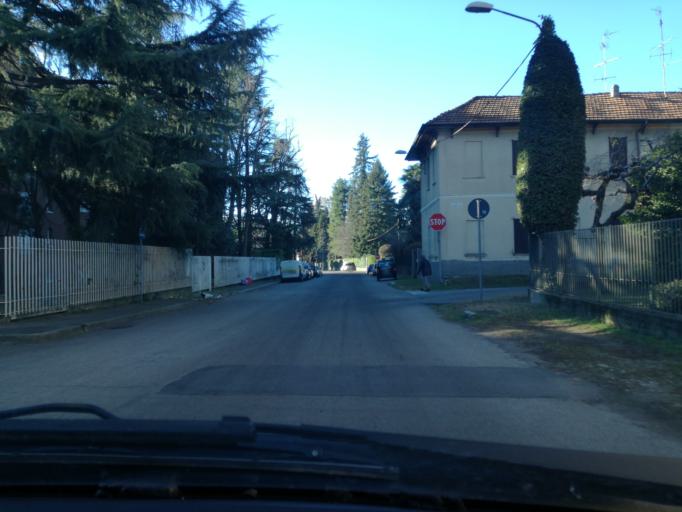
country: IT
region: Lombardy
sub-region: Provincia di Varese
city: Gallarate
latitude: 45.6694
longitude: 8.7966
